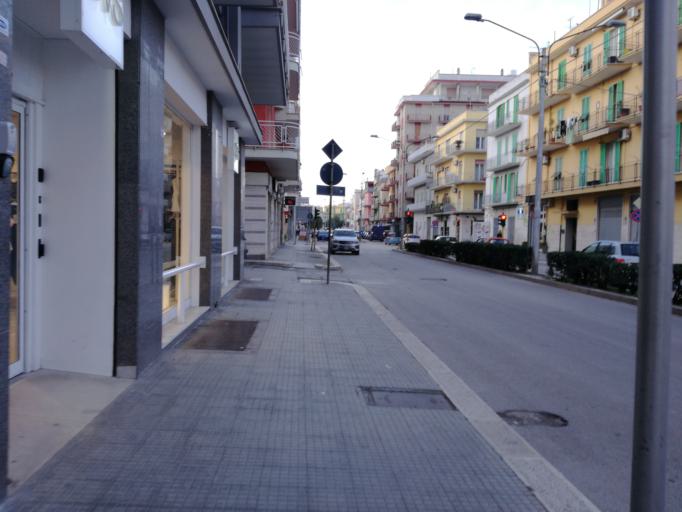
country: IT
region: Apulia
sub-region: Provincia di Bari
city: Corato
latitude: 41.1500
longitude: 16.4086
